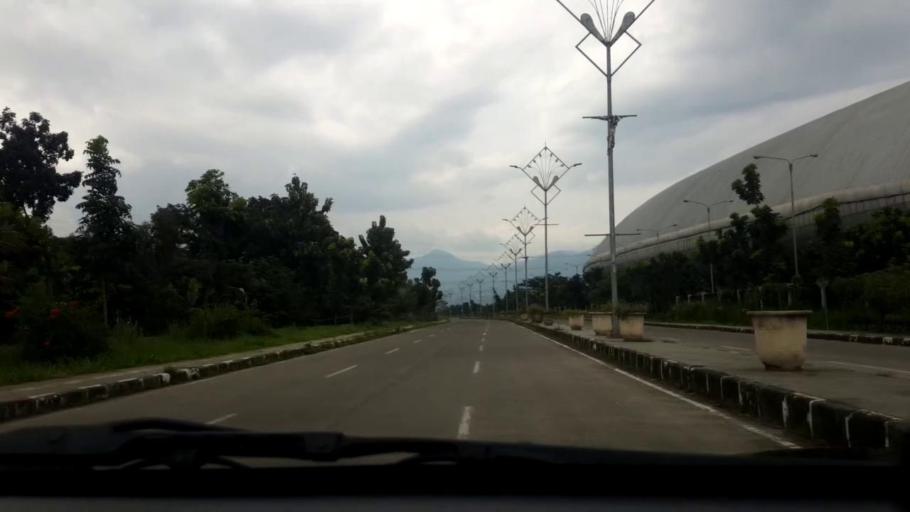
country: ID
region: West Java
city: Cileunyi
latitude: -6.9589
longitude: 107.7103
